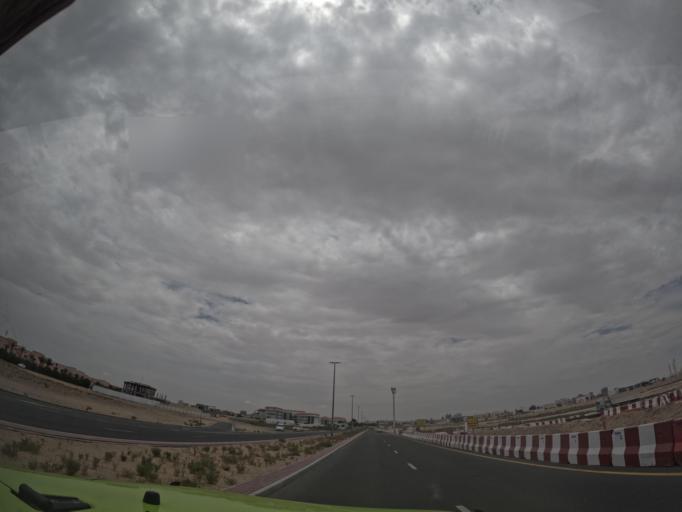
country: AE
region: Ash Shariqah
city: Sharjah
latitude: 25.1567
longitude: 55.3720
